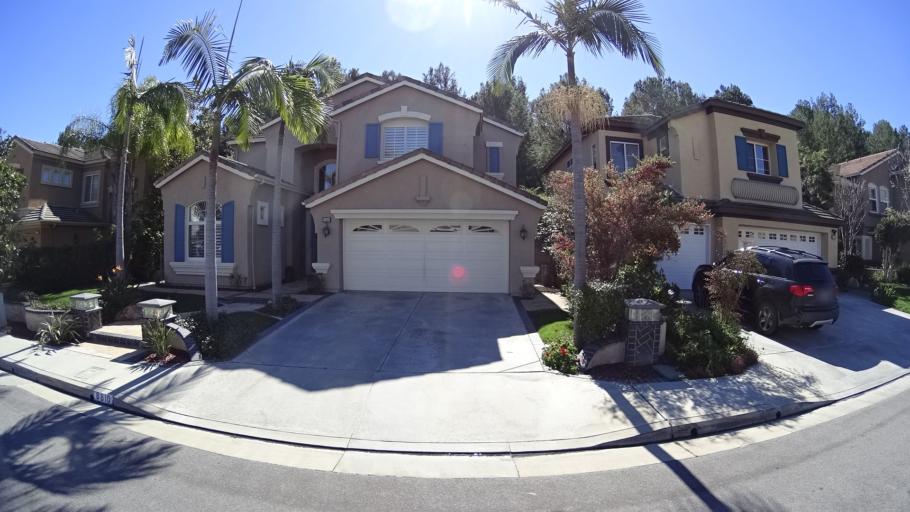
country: US
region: California
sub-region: Orange County
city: Yorba Linda
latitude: 33.8596
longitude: -117.7214
